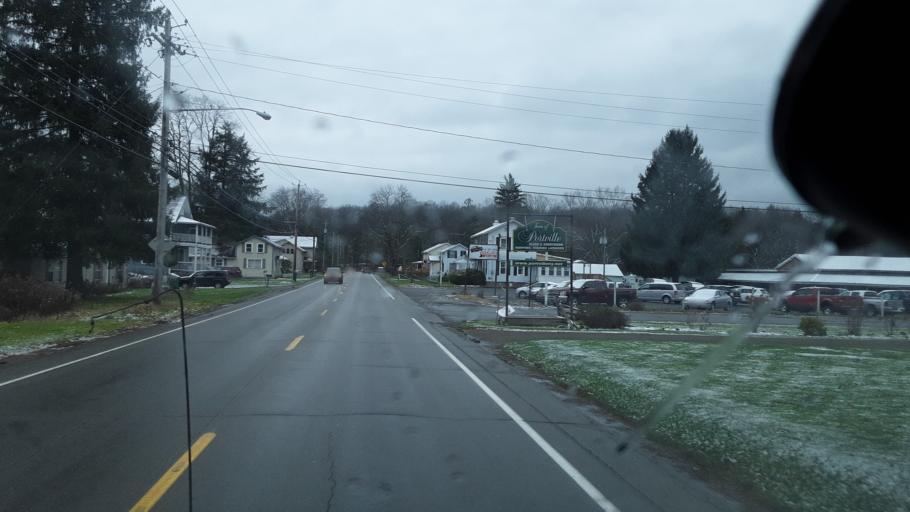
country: US
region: New York
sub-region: Cattaraugus County
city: Portville
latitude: 42.0525
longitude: -78.3569
